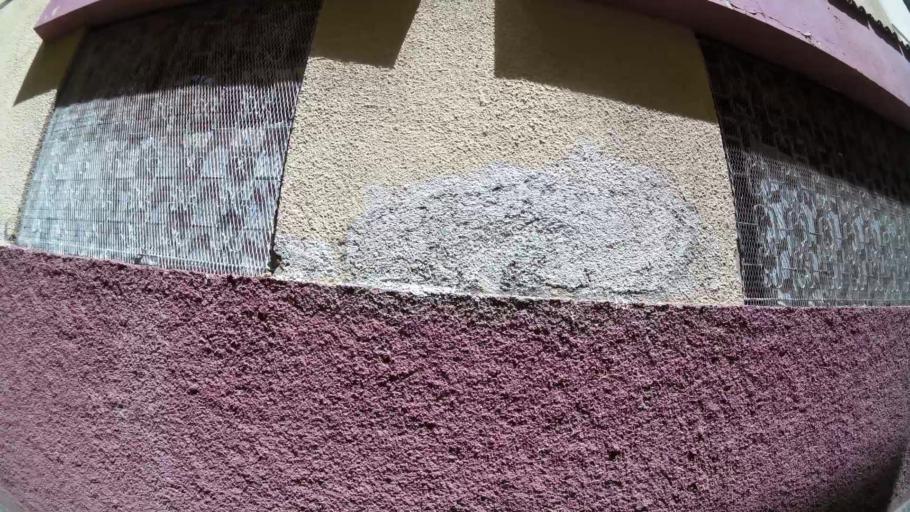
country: MA
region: Fes-Boulemane
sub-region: Fes
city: Fes
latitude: 34.0096
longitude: -4.9869
